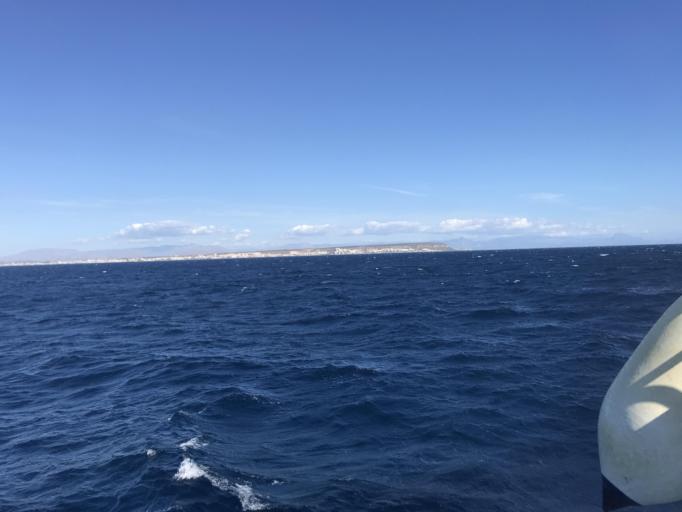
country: ES
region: Valencia
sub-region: Provincia de Alicante
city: Santa Pola
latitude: 38.1308
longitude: -0.5361
